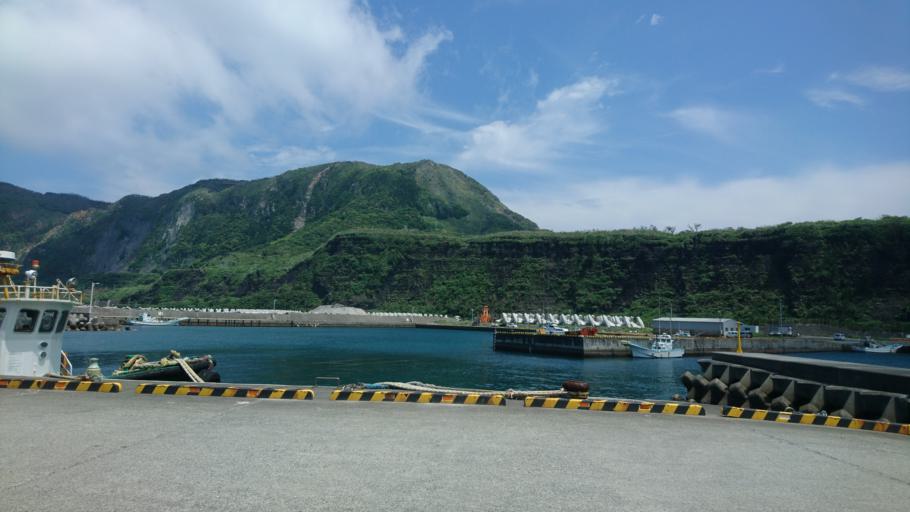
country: JP
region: Shizuoka
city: Shimoda
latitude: 34.4169
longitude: 139.2751
